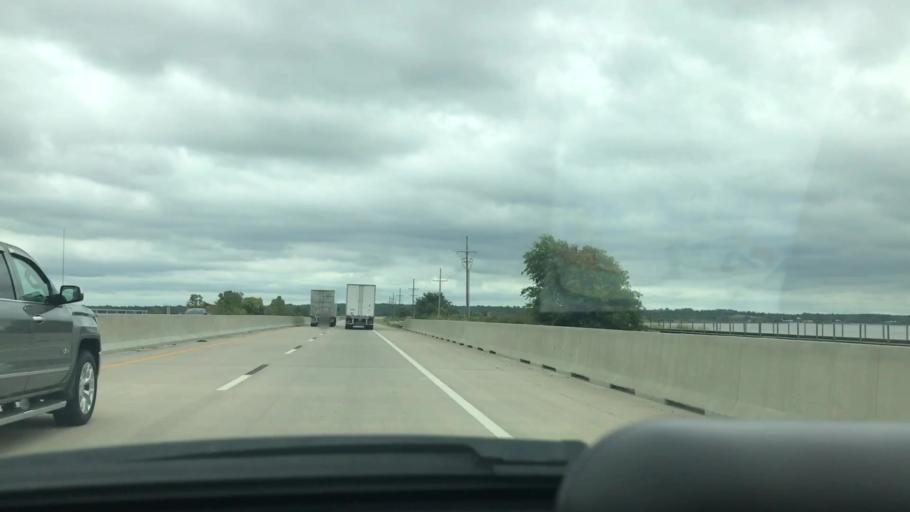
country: US
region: Oklahoma
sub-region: McIntosh County
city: Eufaula
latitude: 35.3322
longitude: -95.5866
